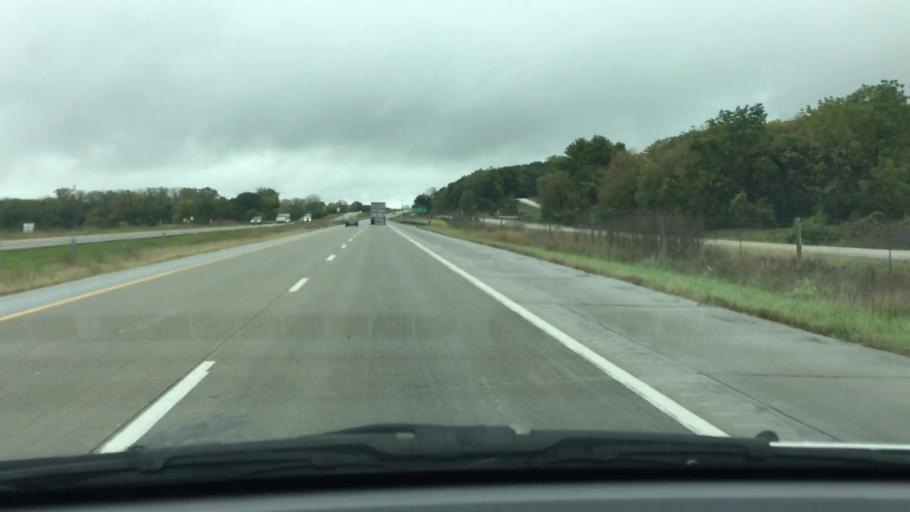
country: US
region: Iowa
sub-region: Jasper County
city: Colfax
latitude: 41.6894
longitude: -93.2630
